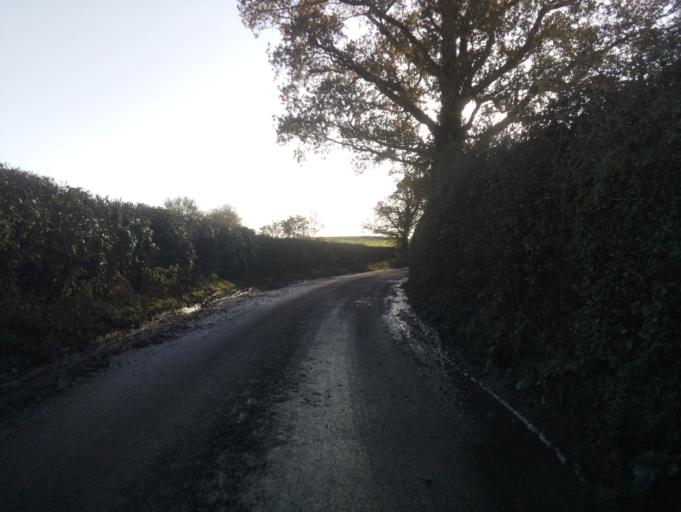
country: GB
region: England
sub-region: Somerset
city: Milborne Port
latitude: 50.9933
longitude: -2.4595
